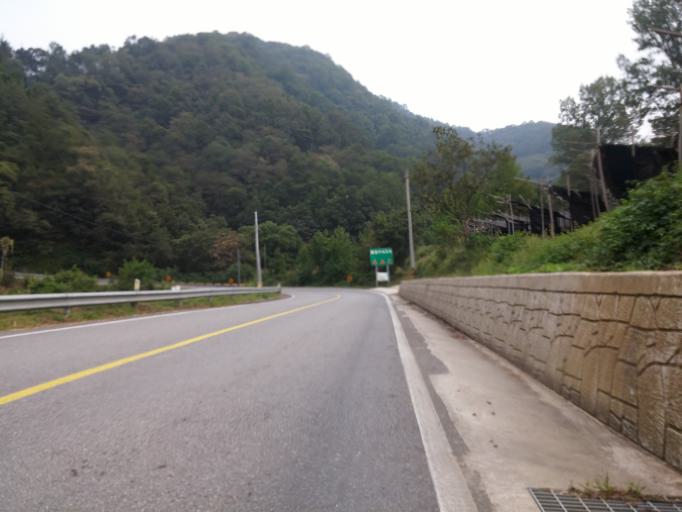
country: KR
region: Chungcheongbuk-do
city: Okcheon
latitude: 36.3928
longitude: 127.6769
